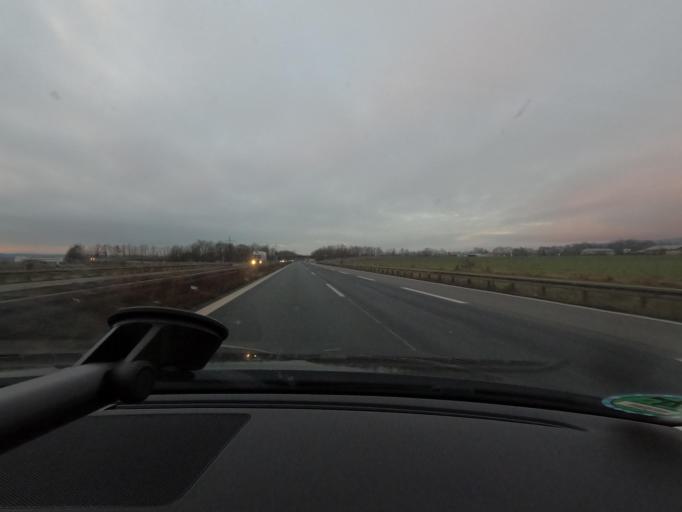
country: DE
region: Bavaria
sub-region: Upper Franconia
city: Buttenheim
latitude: 49.7926
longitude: 11.0287
